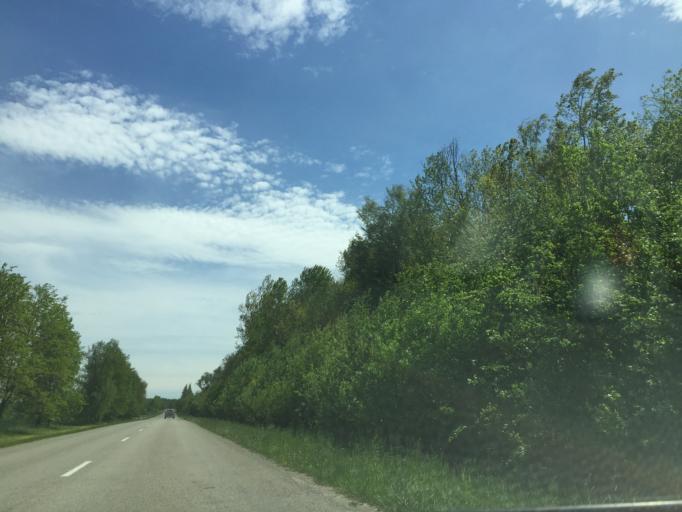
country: LT
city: Linkuva
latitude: 56.0385
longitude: 24.1433
